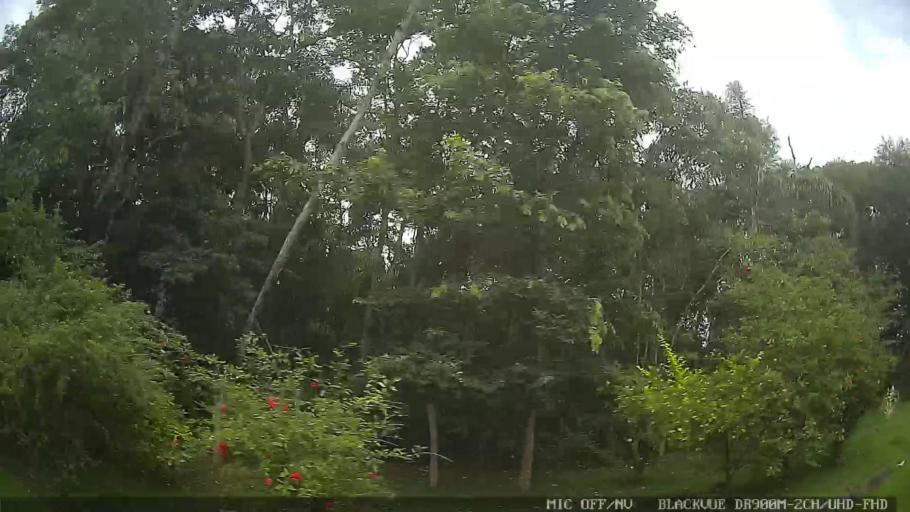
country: BR
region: Sao Paulo
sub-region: Aruja
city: Aruja
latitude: -23.4252
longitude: -46.2287
